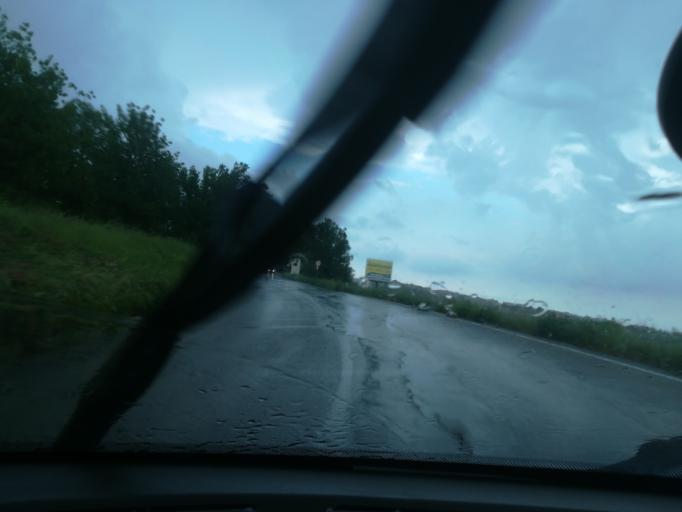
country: IT
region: The Marches
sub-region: Provincia di Macerata
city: Villa Potenza
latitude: 43.2904
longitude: 13.4172
